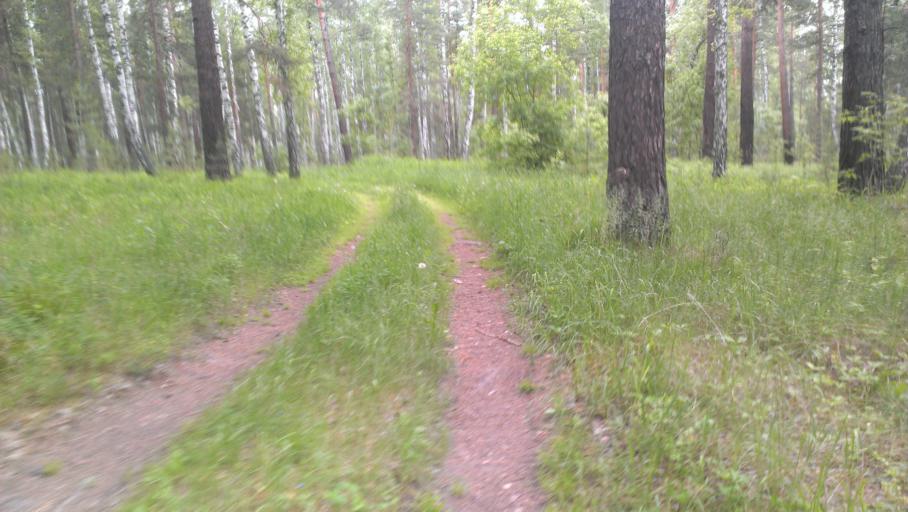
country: RU
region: Altai Krai
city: Sannikovo
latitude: 53.3420
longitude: 84.0464
